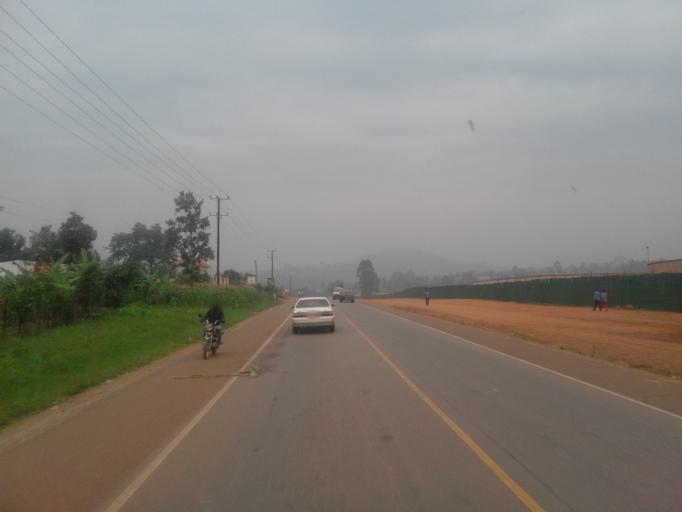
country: UG
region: Central Region
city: Lugazi
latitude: 0.3889
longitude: 32.8509
